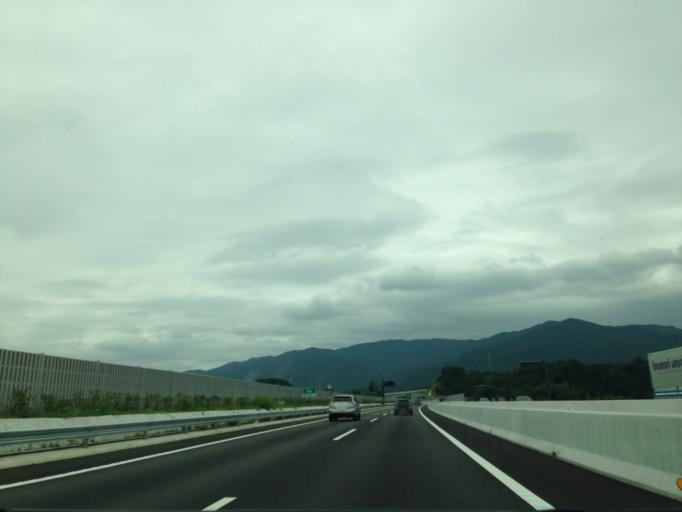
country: JP
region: Aichi
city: Shinshiro
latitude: 34.9211
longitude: 137.5554
